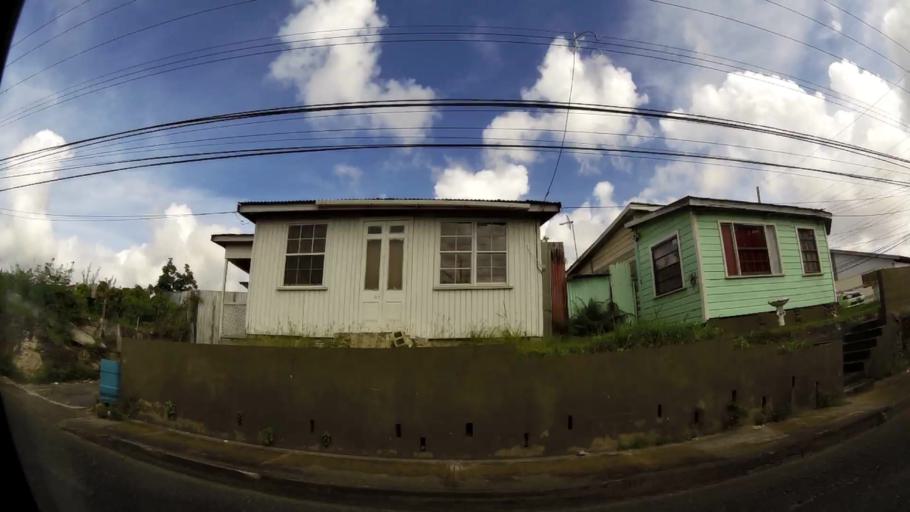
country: BB
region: Saint Michael
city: Bridgetown
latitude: 13.1332
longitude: -59.6056
